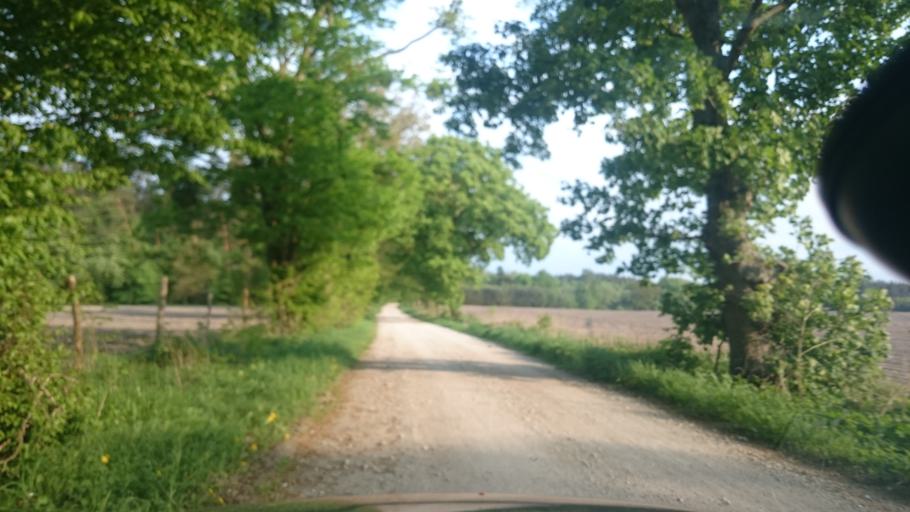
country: PL
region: Kujawsko-Pomorskie
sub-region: Grudziadz
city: Grudziadz
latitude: 53.4515
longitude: 18.8245
